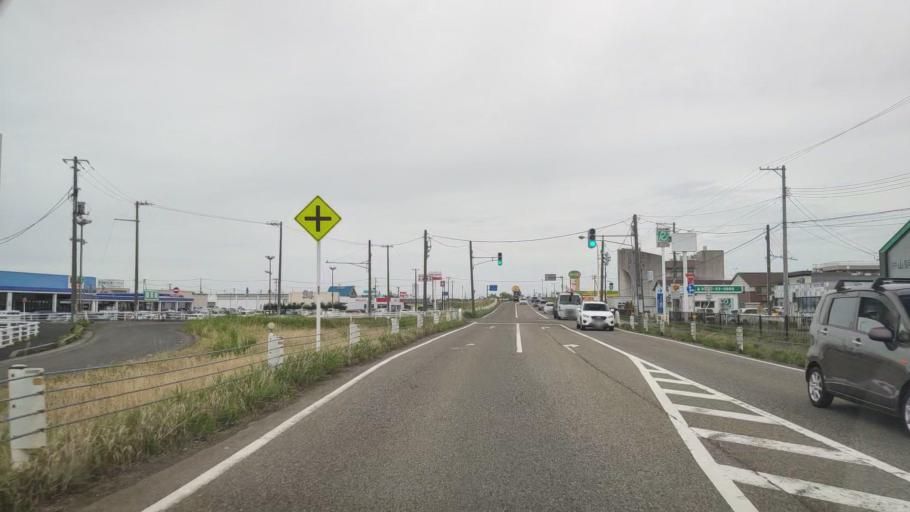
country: JP
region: Niigata
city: Niitsu-honcho
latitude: 37.7890
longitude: 139.1115
